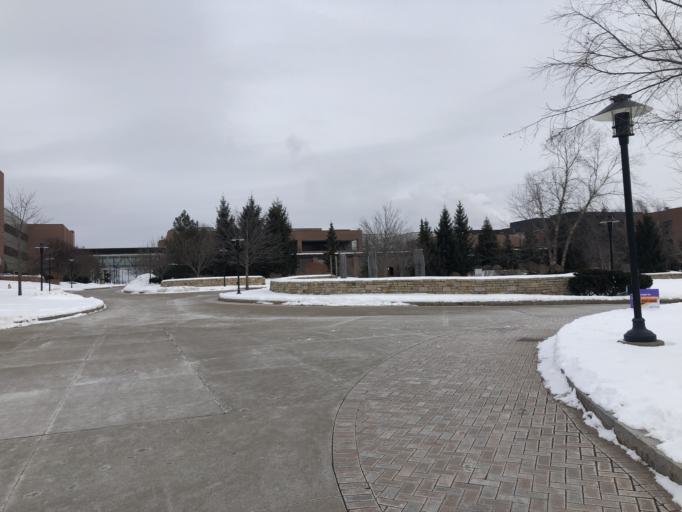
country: US
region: New York
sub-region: Monroe County
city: Scottsville
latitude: 43.0829
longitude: -77.6794
